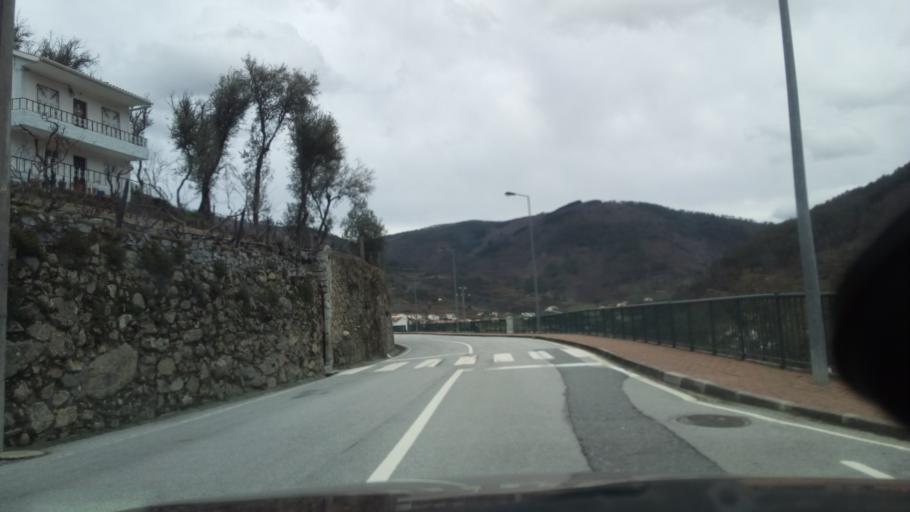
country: PT
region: Guarda
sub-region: Manteigas
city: Manteigas
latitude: 40.3949
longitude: -7.5432
